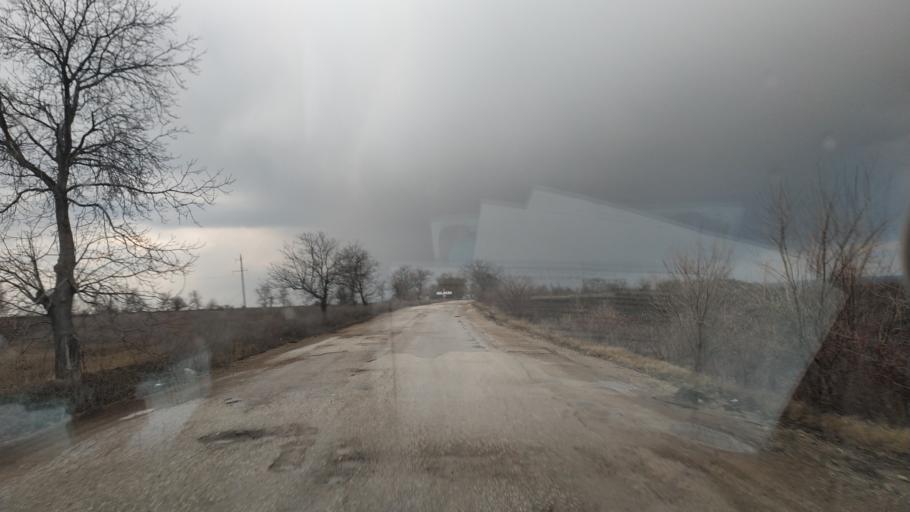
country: MD
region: Telenesti
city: Grigoriopol
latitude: 47.0666
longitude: 29.3000
